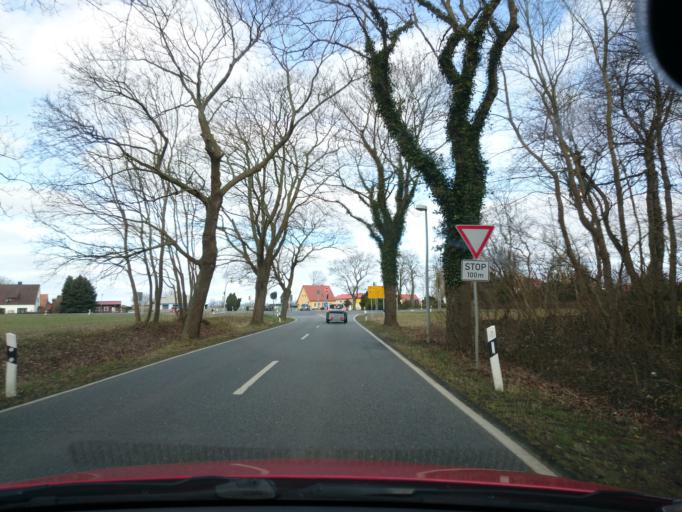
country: DE
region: Mecklenburg-Vorpommern
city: Velgast
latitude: 54.3013
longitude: 12.7908
